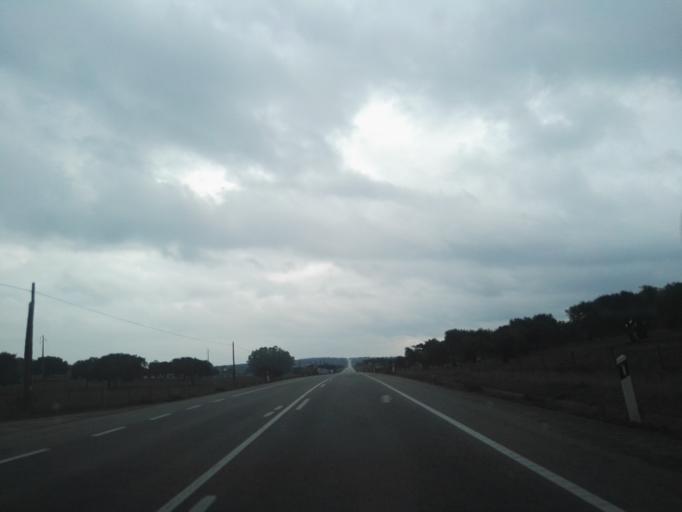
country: PT
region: Portalegre
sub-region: Portalegre
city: Alegrete
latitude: 39.1727
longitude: -7.3346
